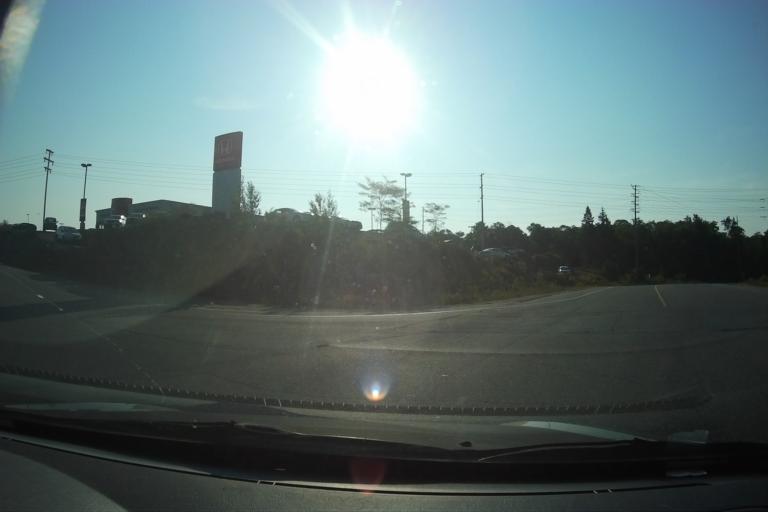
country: CA
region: Ontario
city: Huntsville
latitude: 45.3403
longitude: -79.2238
